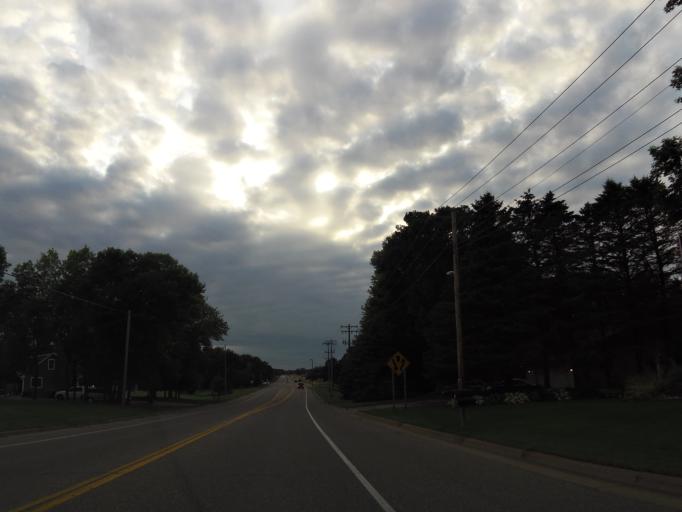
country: US
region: Minnesota
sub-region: Dakota County
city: Lakeville
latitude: 44.6560
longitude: -93.2389
